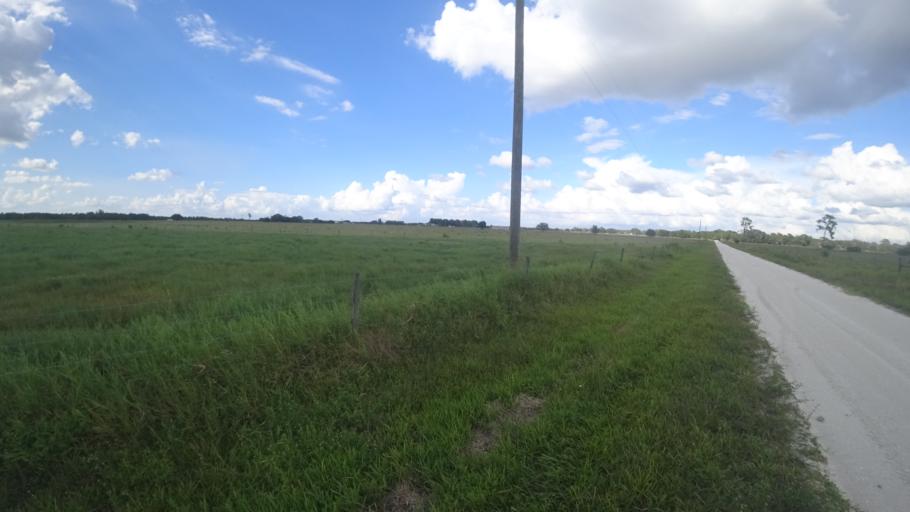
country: US
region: Florida
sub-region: Sarasota County
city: Lake Sarasota
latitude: 27.3350
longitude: -82.1790
